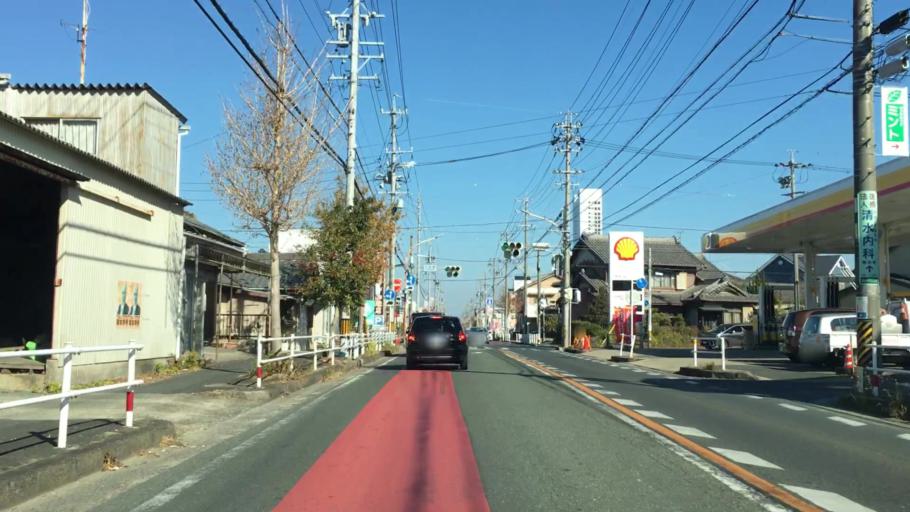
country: JP
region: Aichi
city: Toyohashi
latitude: 34.7396
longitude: 137.3652
